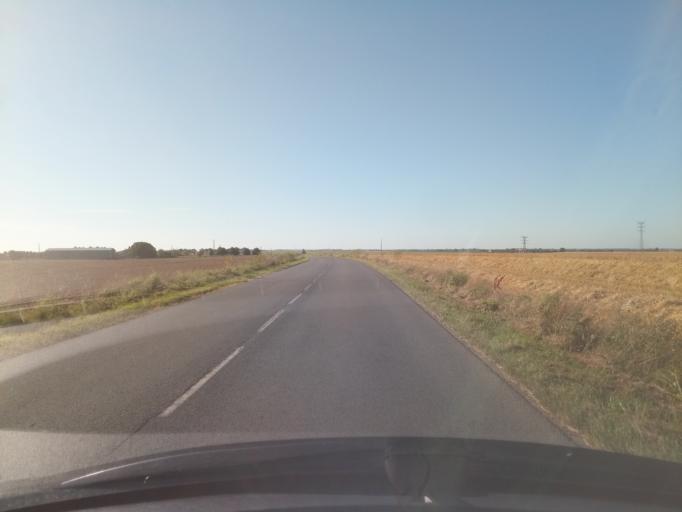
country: FR
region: Poitou-Charentes
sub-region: Departement de la Charente-Maritime
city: Marans
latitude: 46.3008
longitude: -0.9815
